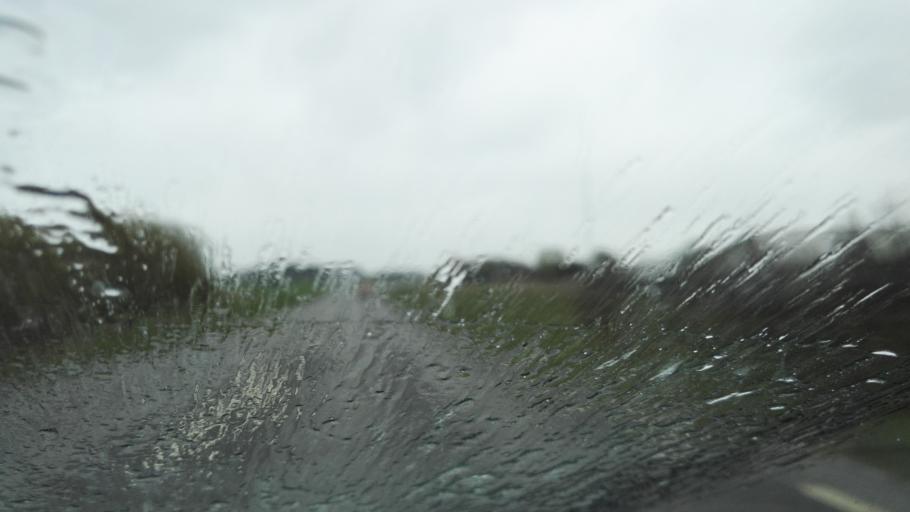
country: SE
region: Skane
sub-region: Ystads Kommun
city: Ystad
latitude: 55.4292
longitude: 13.7736
